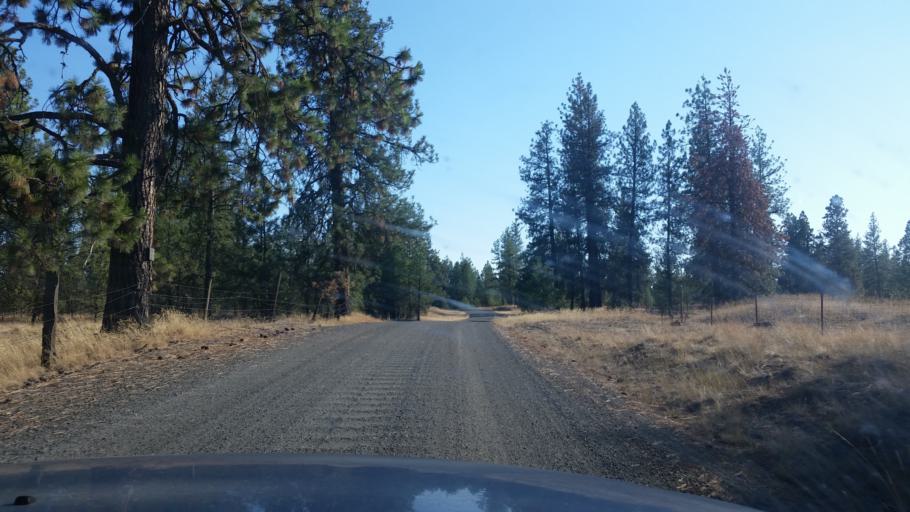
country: US
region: Washington
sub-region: Spokane County
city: Cheney
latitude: 47.4220
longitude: -117.6501
